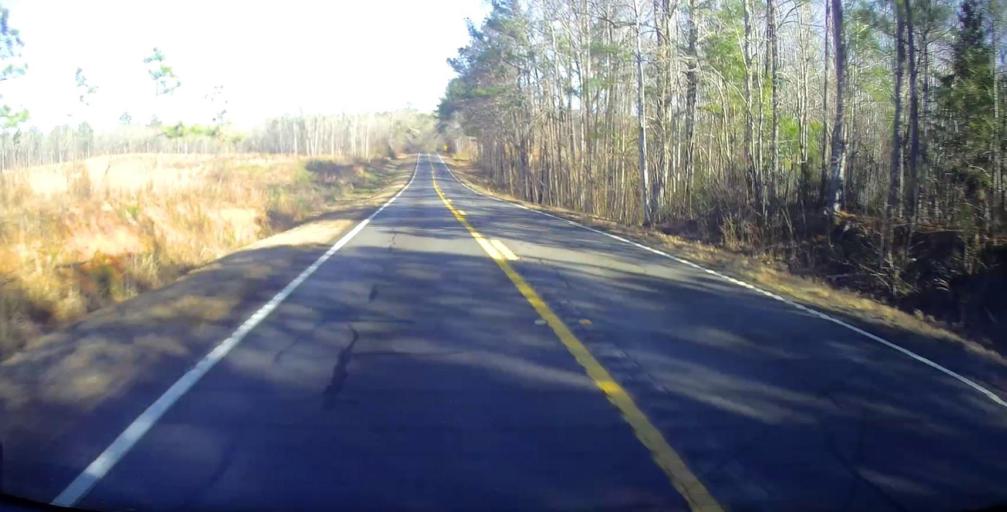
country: US
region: Georgia
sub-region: Talbot County
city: Talbotton
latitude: 32.6723
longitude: -84.4760
